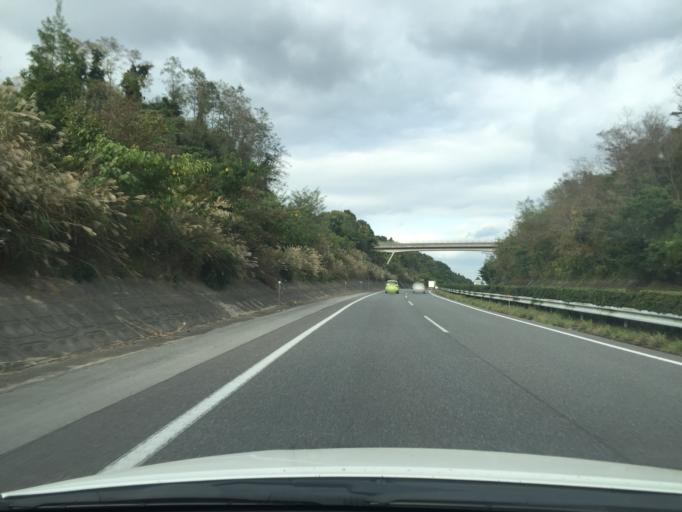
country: JP
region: Fukushima
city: Iwaki
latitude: 37.0511
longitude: 140.8227
